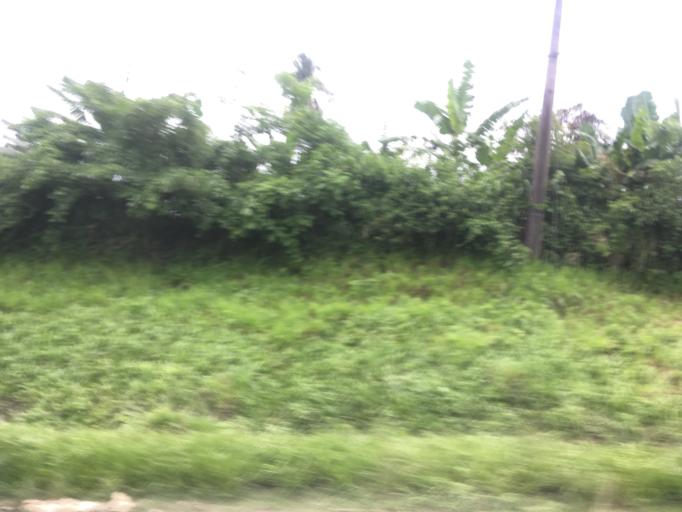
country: CU
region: Villa Clara
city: Esperanza
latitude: 22.4230
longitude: -80.0498
